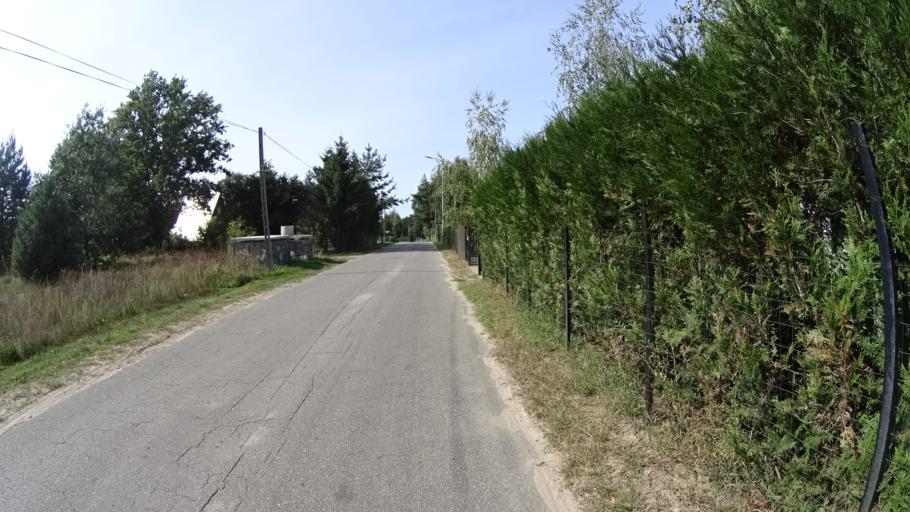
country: PL
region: Masovian Voivodeship
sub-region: Powiat legionowski
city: Serock
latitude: 52.4832
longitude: 21.0825
